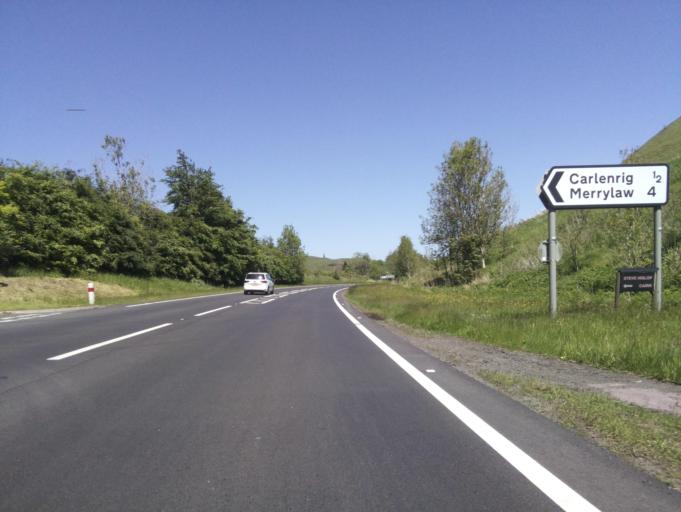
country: GB
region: Scotland
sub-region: The Scottish Borders
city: Hawick
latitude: 55.3391
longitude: -2.9386
